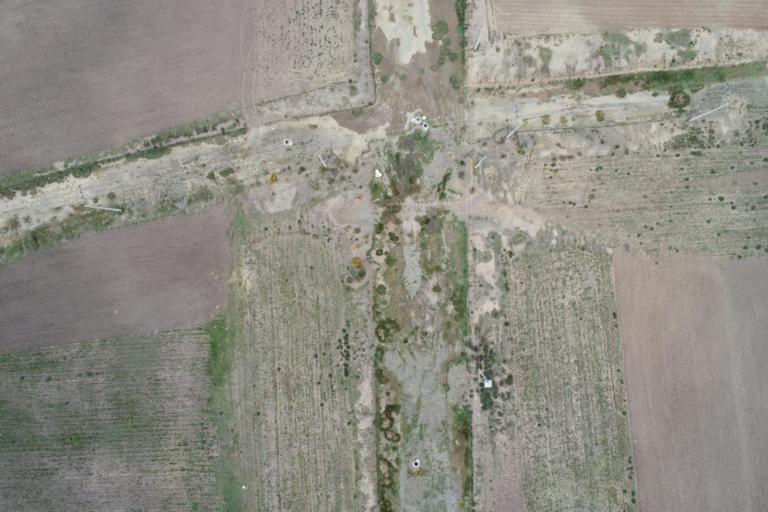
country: BO
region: La Paz
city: La Paz
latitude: -16.5153
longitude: -68.3021
